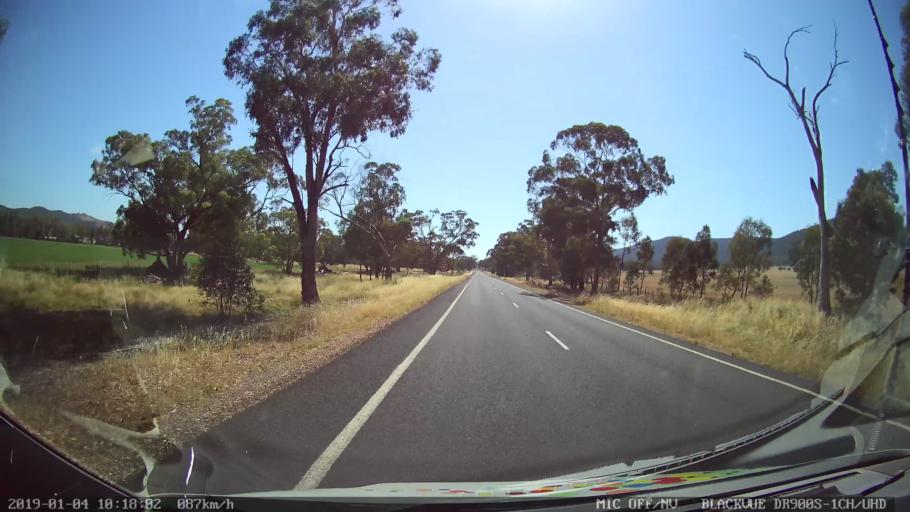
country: AU
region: New South Wales
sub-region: Cabonne
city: Canowindra
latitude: -33.3832
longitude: 148.4605
